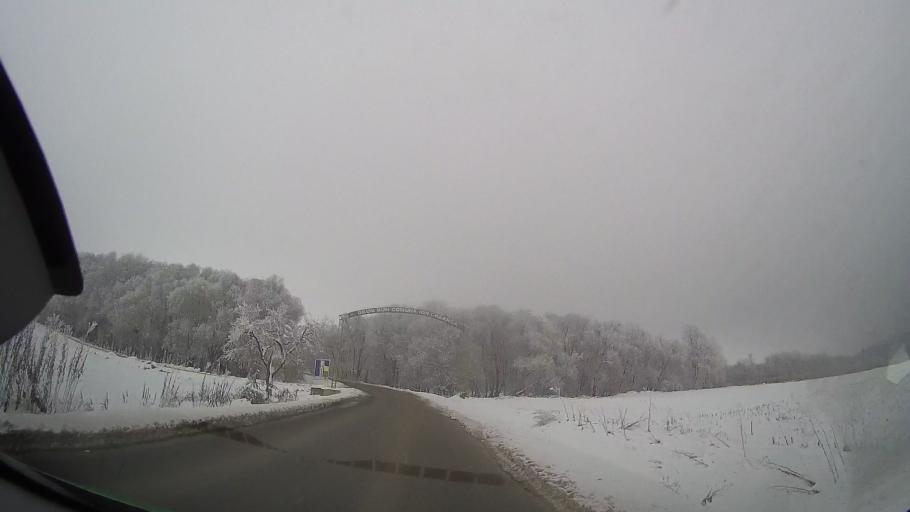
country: RO
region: Neamt
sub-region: Comuna Horia
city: Cotu Vames
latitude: 46.8802
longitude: 26.9735
